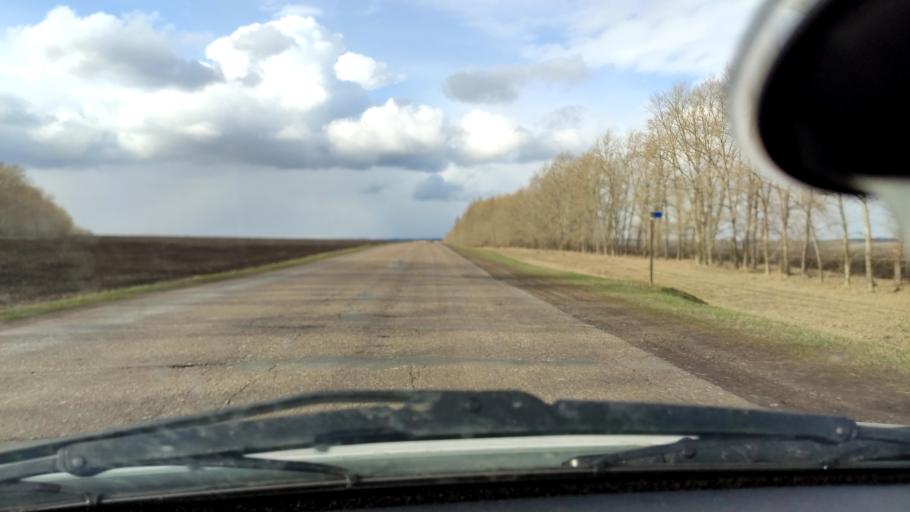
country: RU
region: Bashkortostan
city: Buzdyak
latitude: 54.7491
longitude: 54.5645
